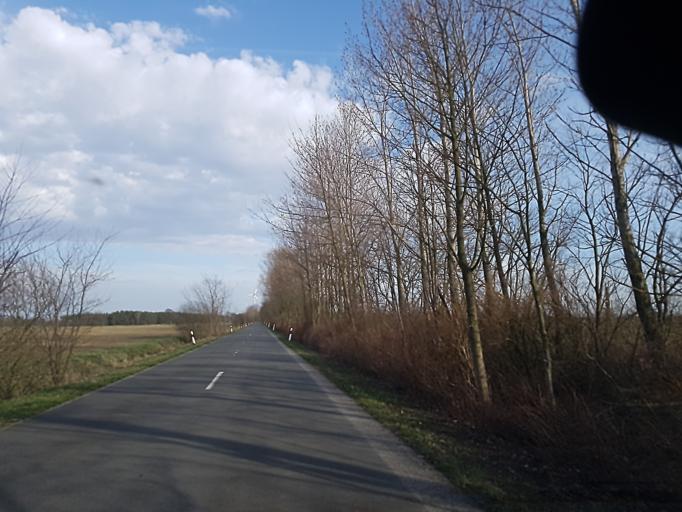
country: DE
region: Brandenburg
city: Falkenberg
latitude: 51.5475
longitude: 13.3012
